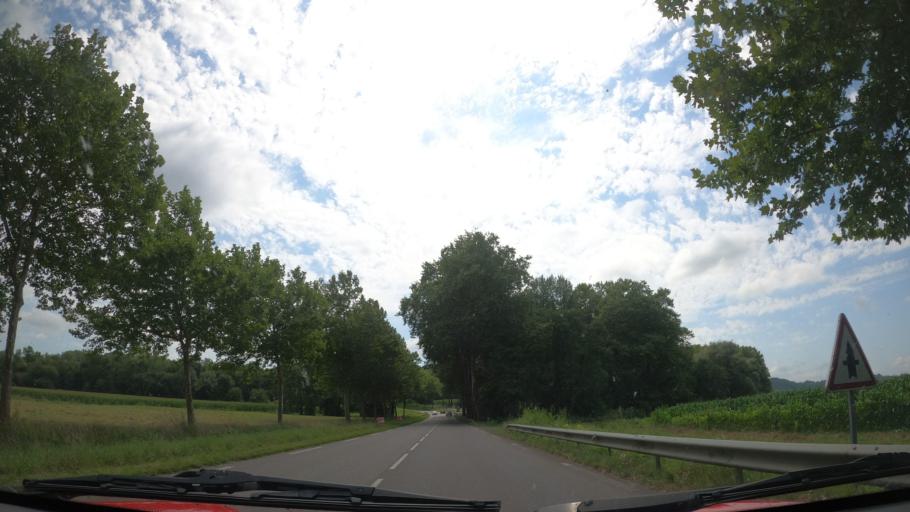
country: FR
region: Aquitaine
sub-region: Departement des Landes
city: Peyrehorade
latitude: 43.5335
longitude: -1.1098
